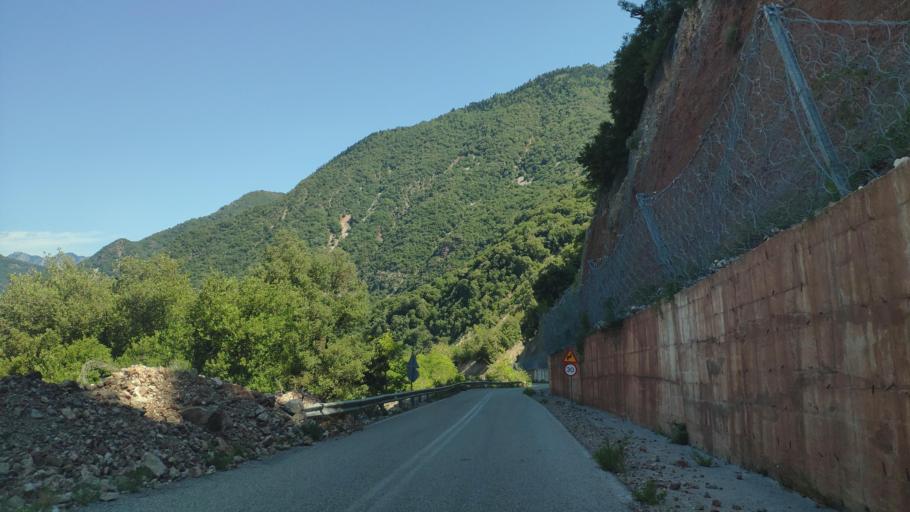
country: GR
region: Central Greece
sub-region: Nomos Evrytanias
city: Kerasochori
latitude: 39.0176
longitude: 21.5994
